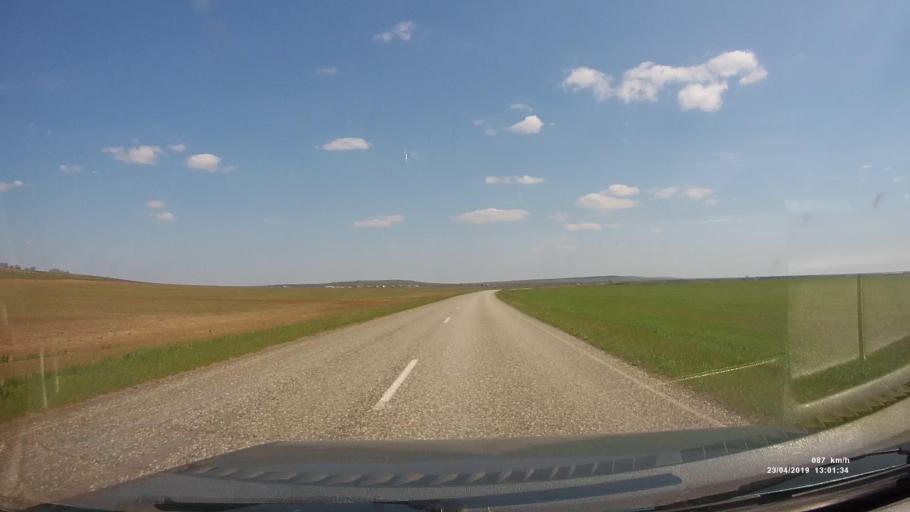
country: RU
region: Kalmykiya
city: Yashalta
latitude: 46.6038
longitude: 42.6546
